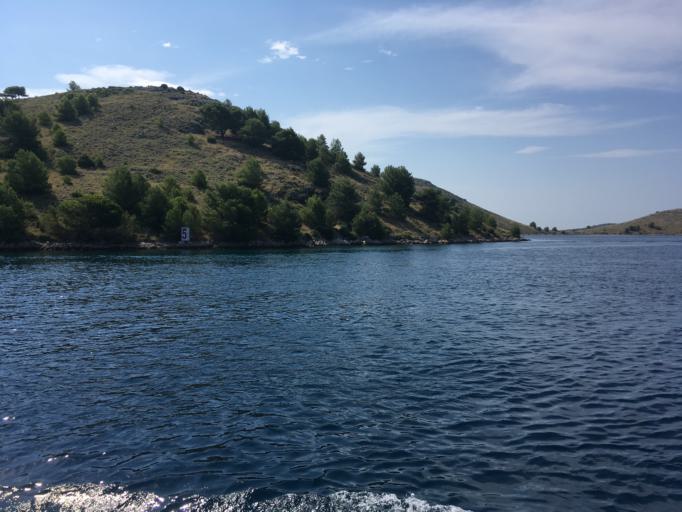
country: HR
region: Zadarska
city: Sali
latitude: 43.8886
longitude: 15.2132
